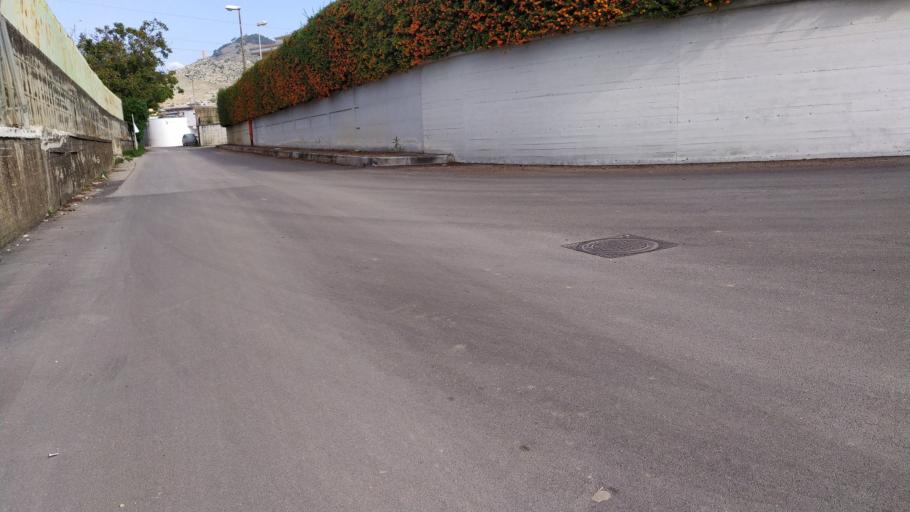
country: IT
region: Campania
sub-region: Provincia di Caserta
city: Maddaloni
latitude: 41.0282
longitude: 14.3968
